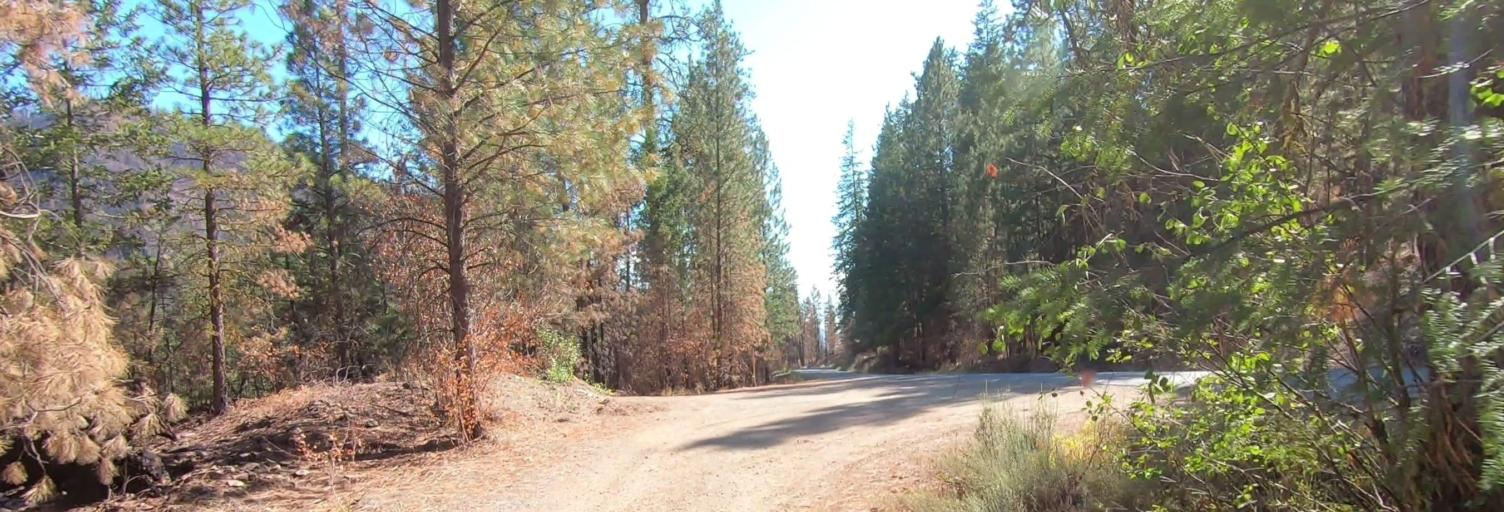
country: US
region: Washington
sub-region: Okanogan County
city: Brewster
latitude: 48.5774
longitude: -120.1756
